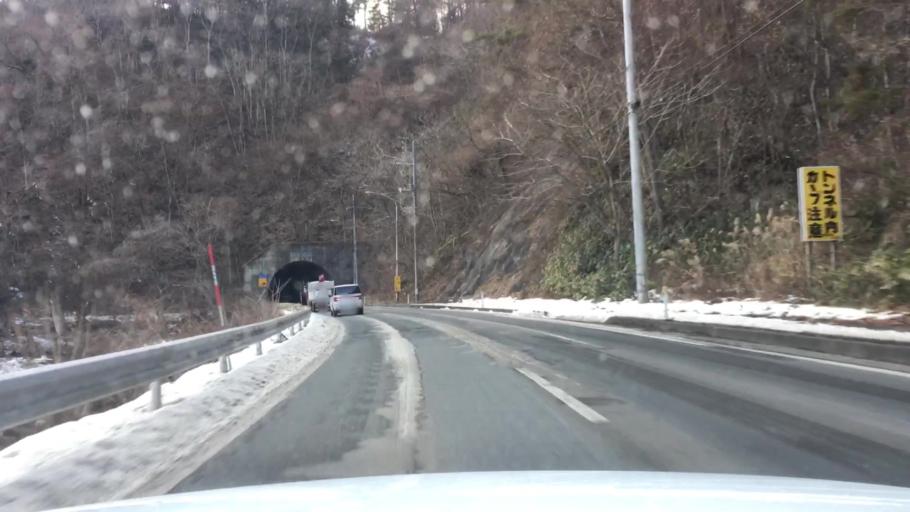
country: JP
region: Iwate
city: Morioka-shi
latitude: 39.6774
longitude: 141.2249
